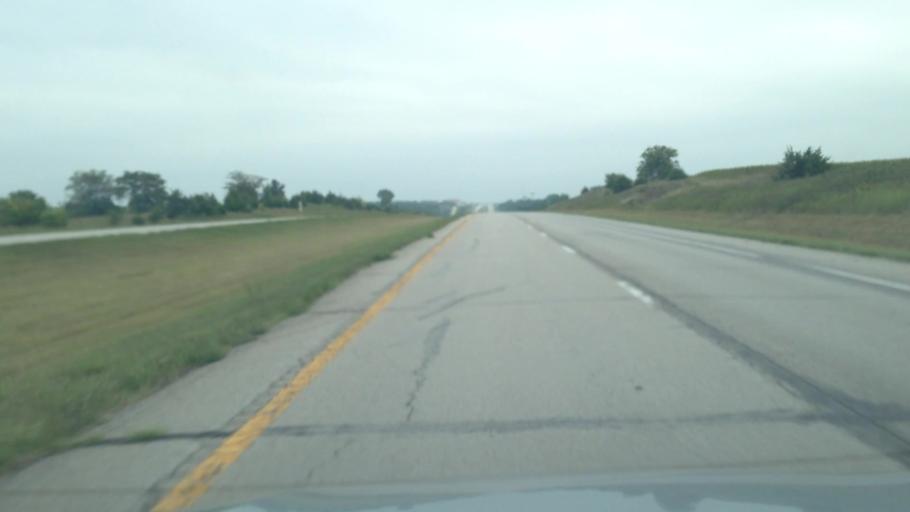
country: US
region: Iowa
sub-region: Decatur County
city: Lamoni
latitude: 40.4912
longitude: -93.9699
